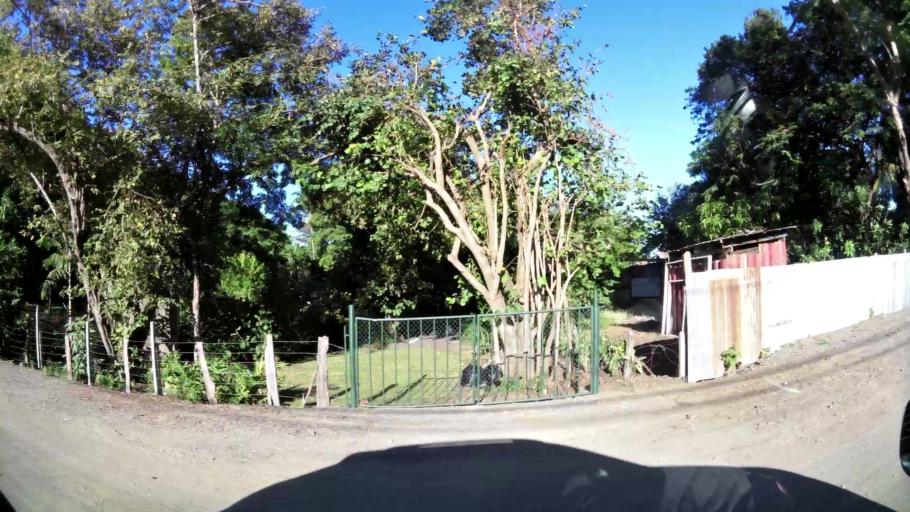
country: CR
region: Guanacaste
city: Sardinal
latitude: 10.5757
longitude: -85.6771
